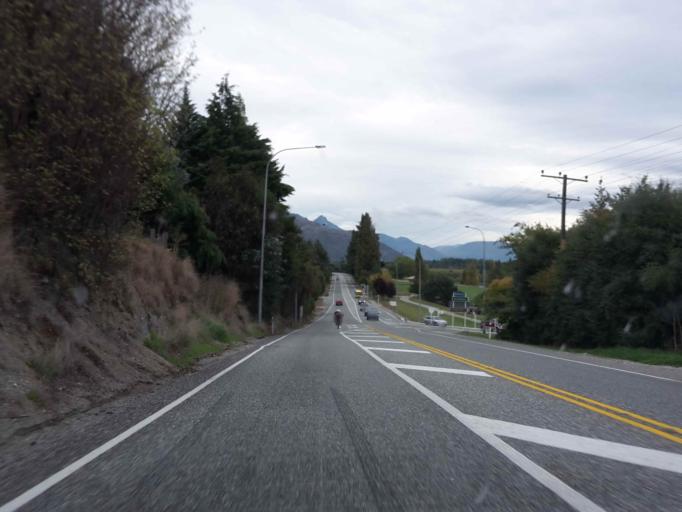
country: NZ
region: Otago
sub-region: Queenstown-Lakes District
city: Arrowtown
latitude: -44.9871
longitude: 168.8161
